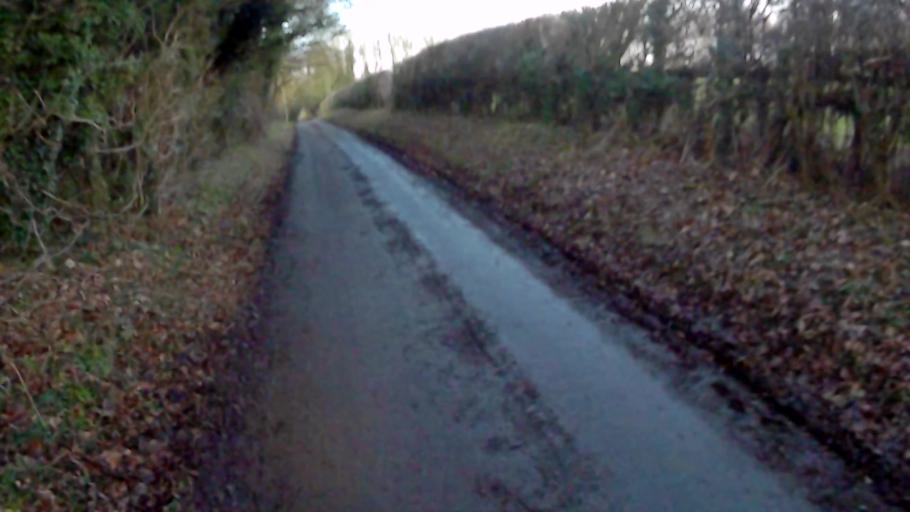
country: GB
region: England
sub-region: Hampshire
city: Overton
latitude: 51.2496
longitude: -1.2169
